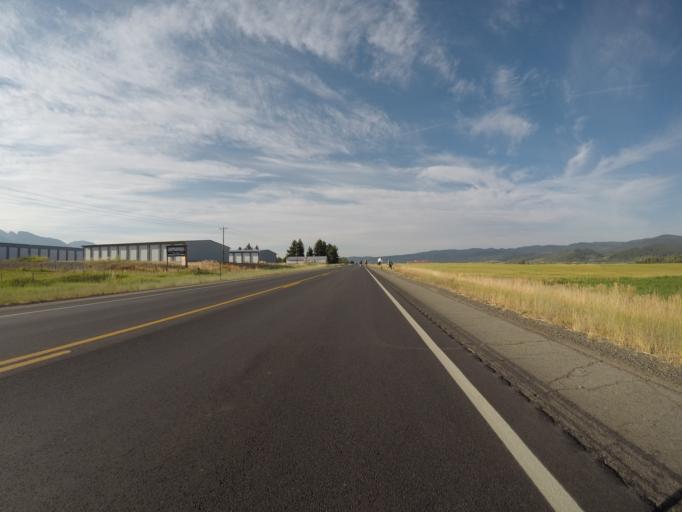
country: US
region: Wyoming
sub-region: Lincoln County
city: Afton
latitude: 42.9772
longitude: -111.0124
